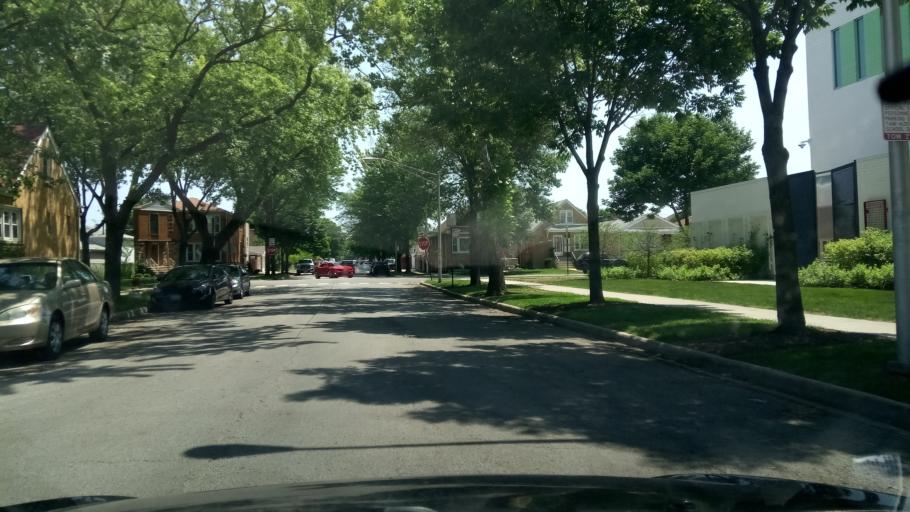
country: US
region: Illinois
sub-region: Cook County
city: Hometown
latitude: 41.7841
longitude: -87.7265
